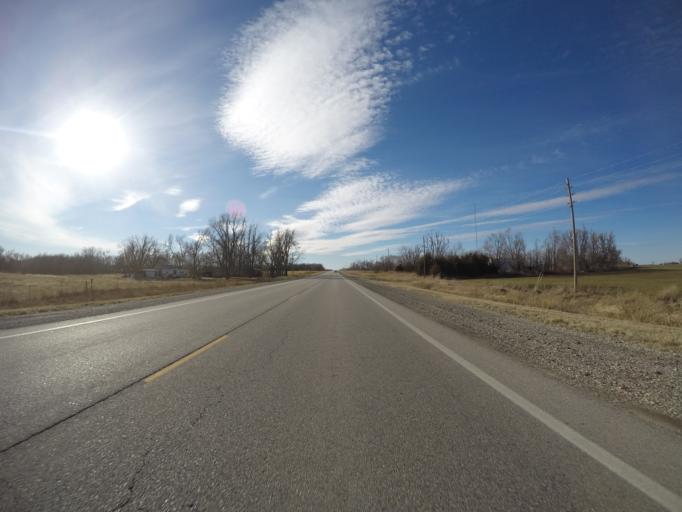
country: US
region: Kansas
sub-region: McPherson County
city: McPherson
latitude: 38.3771
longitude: -97.4955
